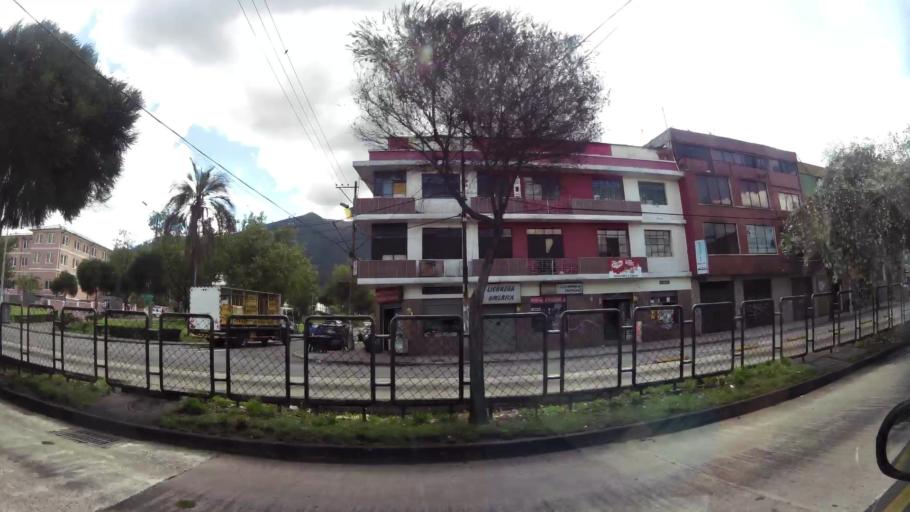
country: EC
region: Pichincha
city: Quito
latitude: -0.1954
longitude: -78.4992
